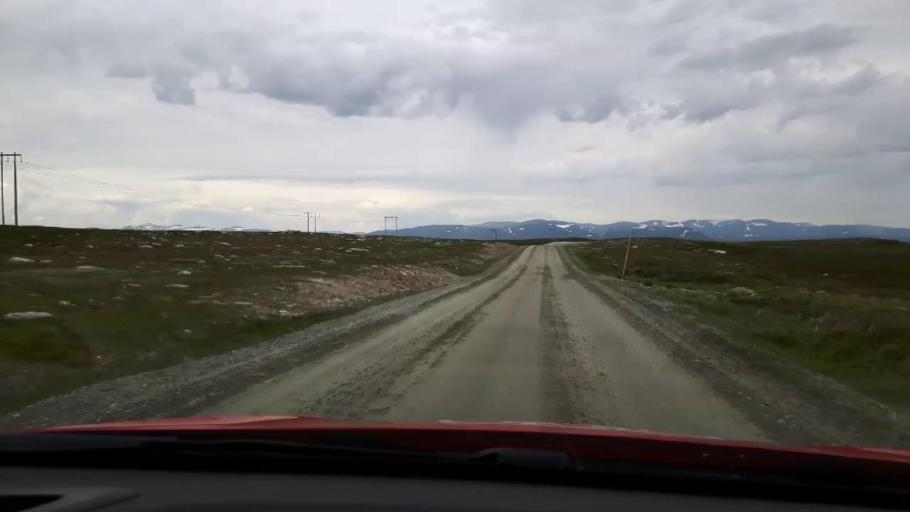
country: SE
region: Jaemtland
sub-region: Are Kommun
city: Are
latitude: 62.7505
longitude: 12.7488
